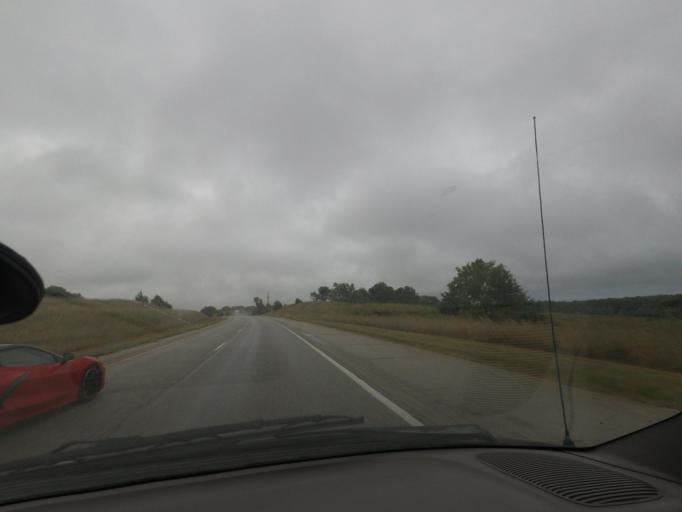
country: US
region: Illinois
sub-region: Pike County
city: Barry
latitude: 39.7303
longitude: -91.1234
